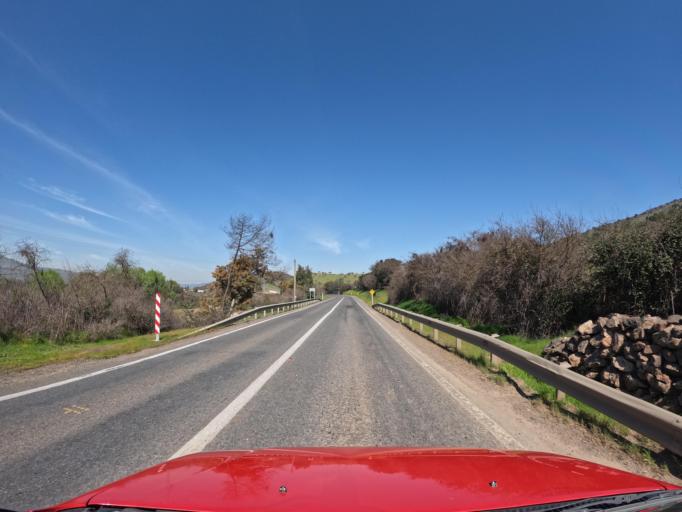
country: CL
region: Maule
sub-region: Provincia de Curico
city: Rauco
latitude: -35.0733
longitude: -71.6265
